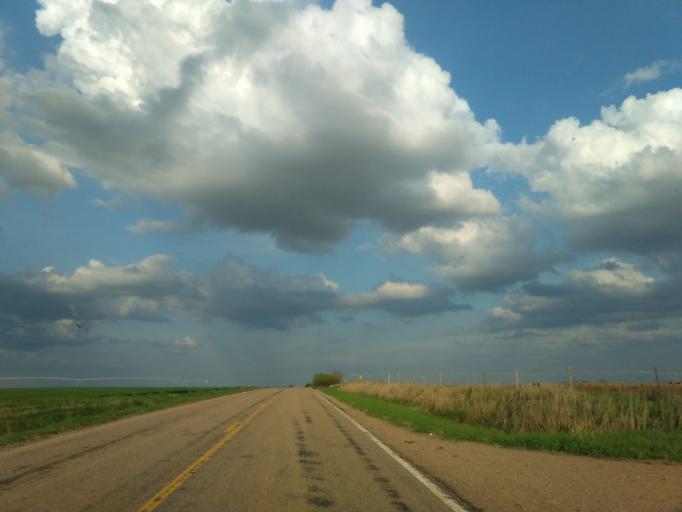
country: US
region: Nebraska
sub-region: Webster County
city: Red Cloud
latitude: 40.1759
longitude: -98.5075
